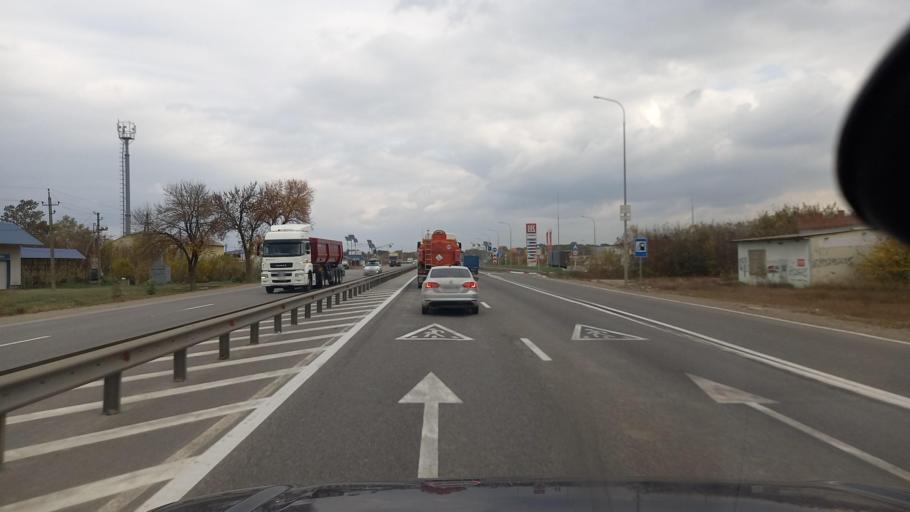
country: RU
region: Adygeya
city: Enem
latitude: 44.9079
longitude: 38.8803
